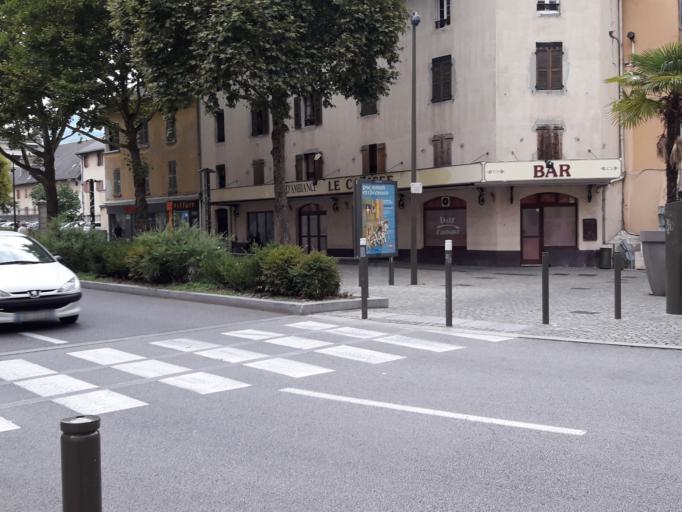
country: FR
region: Rhone-Alpes
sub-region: Departement de la Savoie
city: Chambery
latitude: 45.5660
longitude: 5.9257
